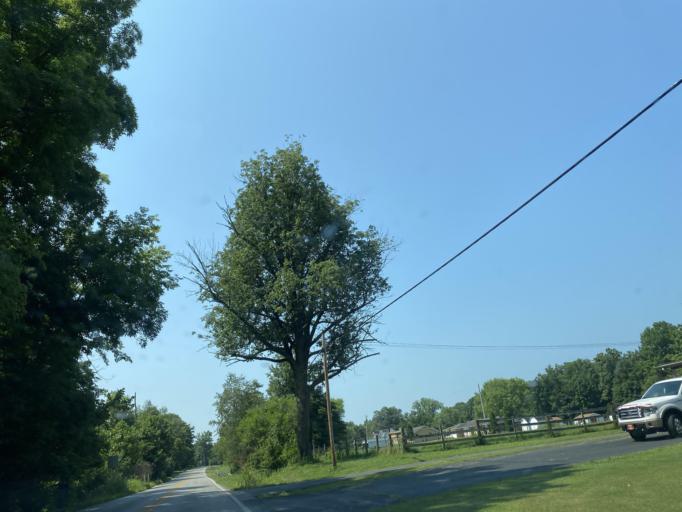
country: US
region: Kentucky
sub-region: Campbell County
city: Claryville
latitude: 38.8853
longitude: -84.4480
